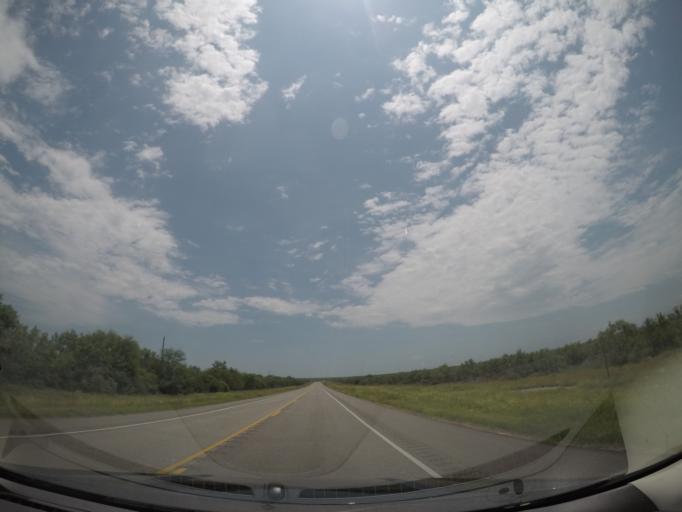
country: US
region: Texas
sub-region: Kinney County
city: Brackettville
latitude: 29.2698
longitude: -100.2654
